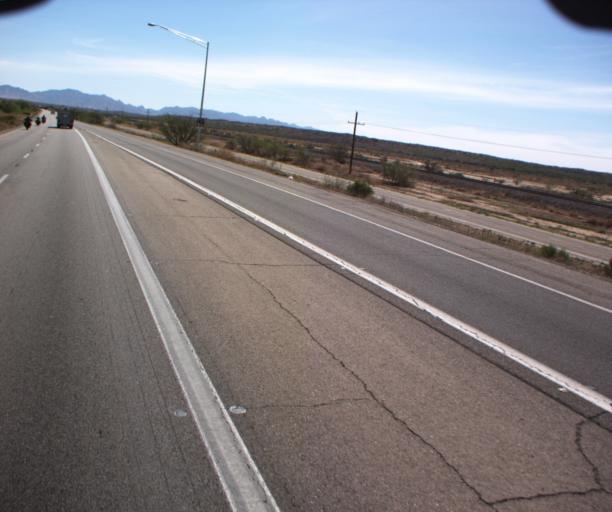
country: US
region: Arizona
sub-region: Cochise County
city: Benson
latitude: 31.9652
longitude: -110.2668
